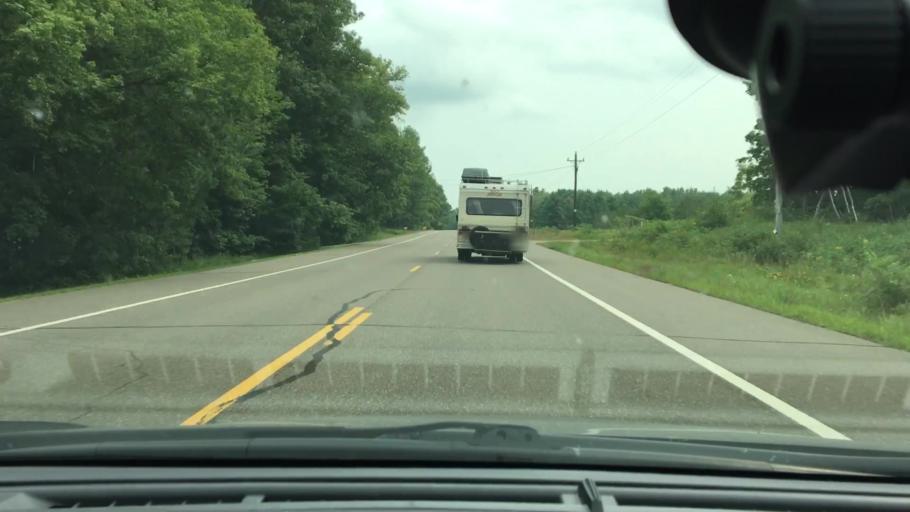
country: US
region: Minnesota
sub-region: Crow Wing County
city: Crosby
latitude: 46.4102
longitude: -93.8422
